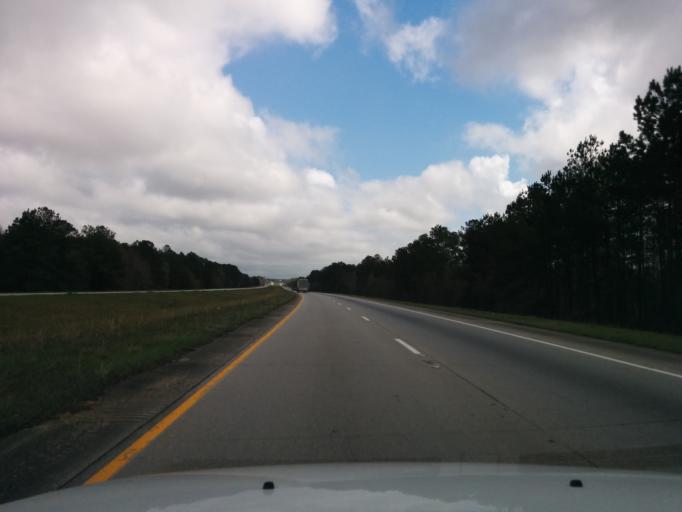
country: US
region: Georgia
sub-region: Emanuel County
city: Swainsboro
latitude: 32.4079
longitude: -82.3469
